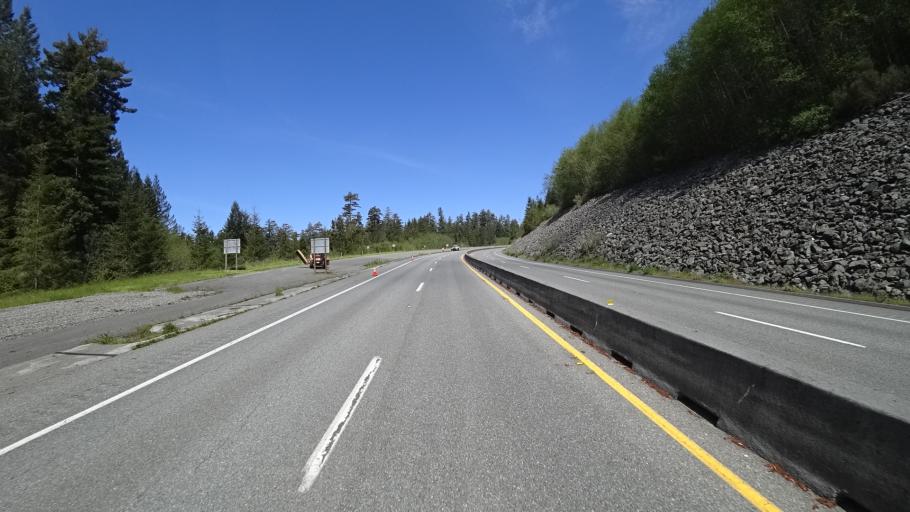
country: US
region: California
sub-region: Humboldt County
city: Westhaven-Moonstone
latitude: 41.3749
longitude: -123.9934
